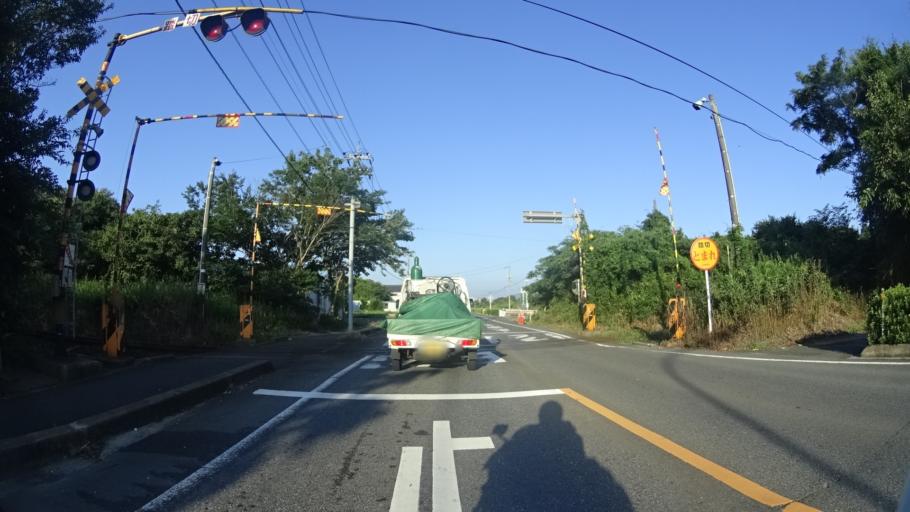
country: JP
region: Shimane
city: Sakaiminato
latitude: 35.5221
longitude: 133.2361
